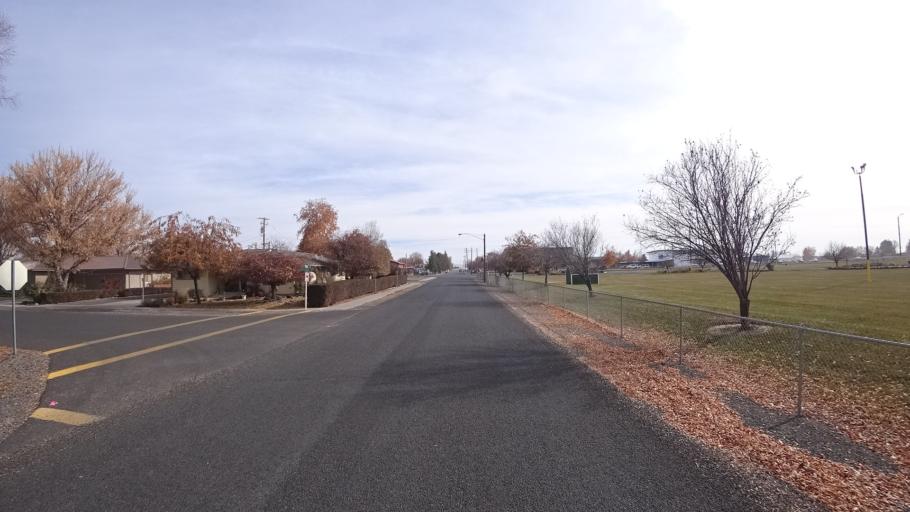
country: US
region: California
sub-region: Siskiyou County
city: Tulelake
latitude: 41.9510
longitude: -121.4782
